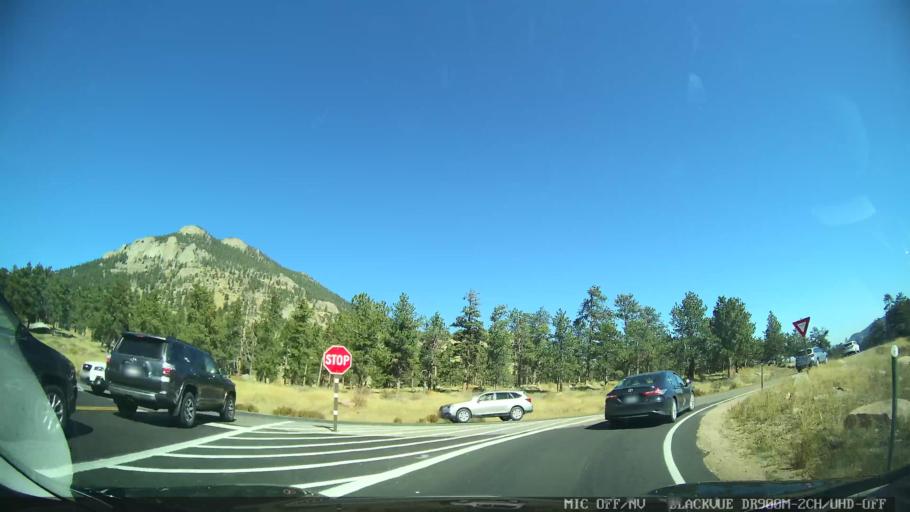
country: US
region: Colorado
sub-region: Larimer County
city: Estes Park
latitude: 40.3658
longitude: -105.5856
